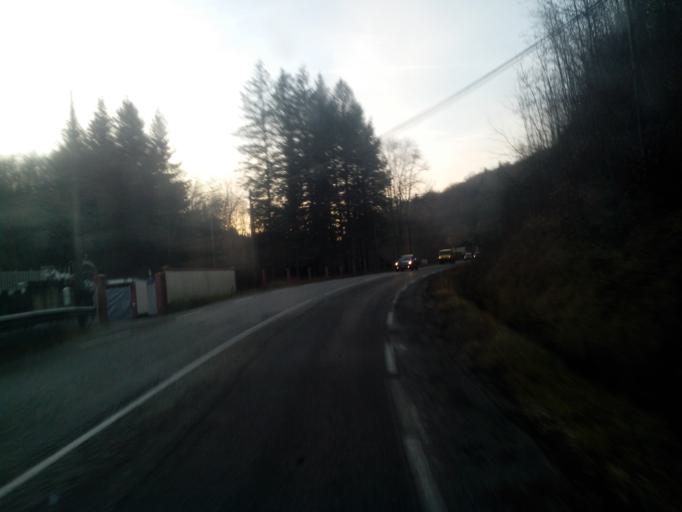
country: FR
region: Midi-Pyrenees
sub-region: Departement de l'Ariege
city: Lavelanet
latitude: 42.9121
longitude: 1.7841
